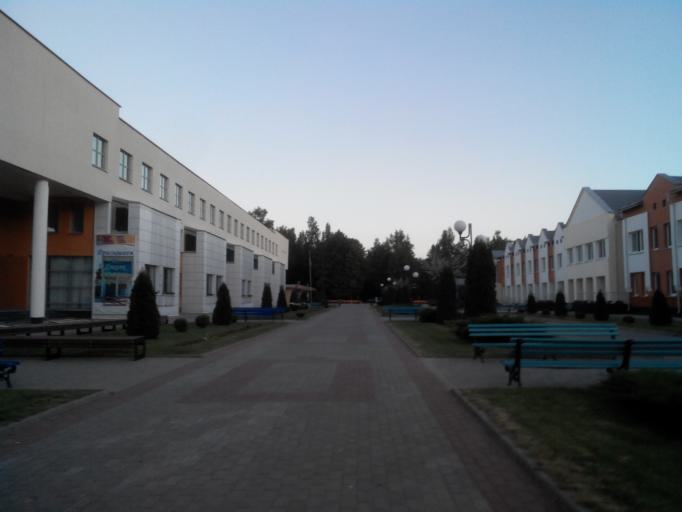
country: BY
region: Minsk
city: Narach
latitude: 54.8337
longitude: 26.7129
